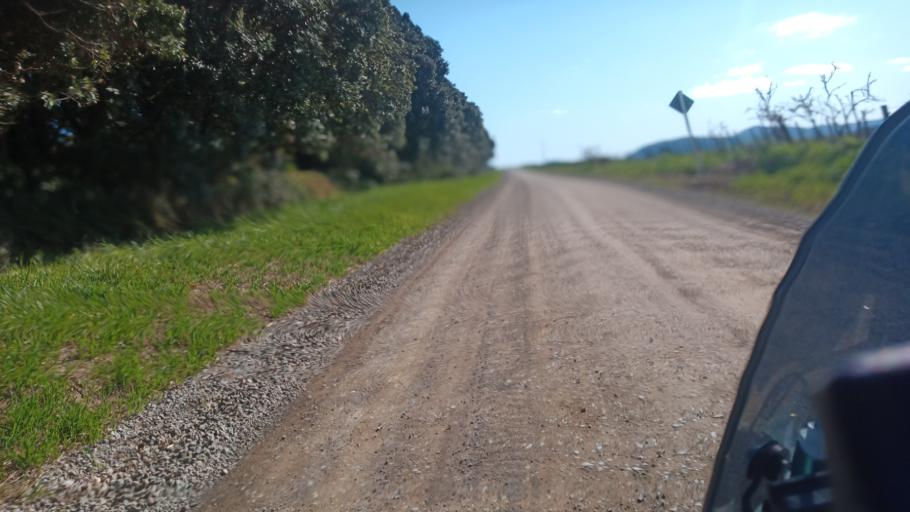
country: NZ
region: Gisborne
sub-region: Gisborne District
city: Gisborne
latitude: -39.1311
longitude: 177.9487
